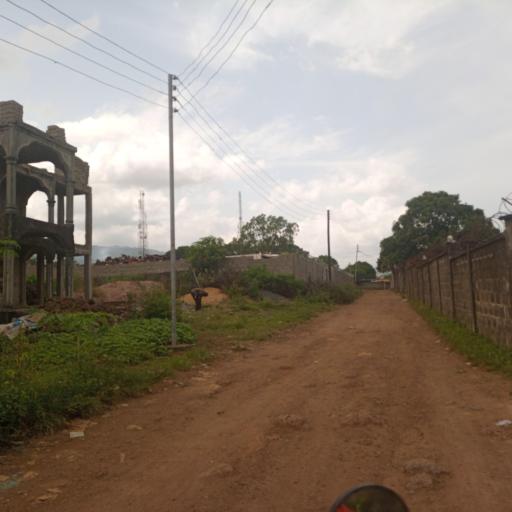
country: SL
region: Western Area
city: Hastings
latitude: 8.3945
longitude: -13.1421
